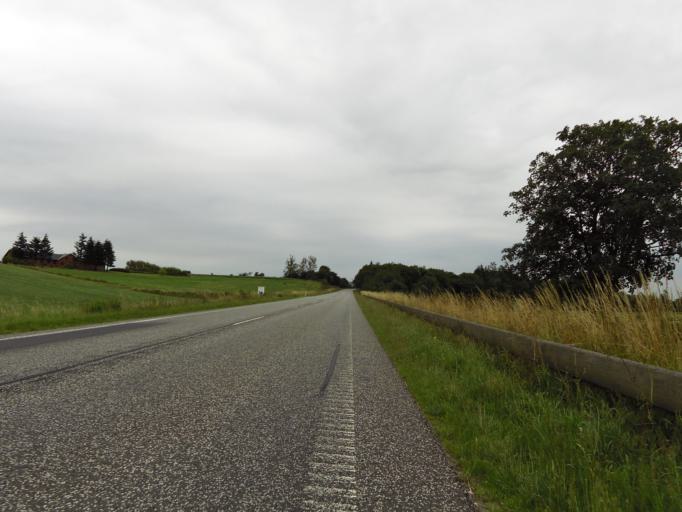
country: DK
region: South Denmark
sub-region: Tonder Kommune
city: Logumkloster
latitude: 55.1172
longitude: 8.9577
